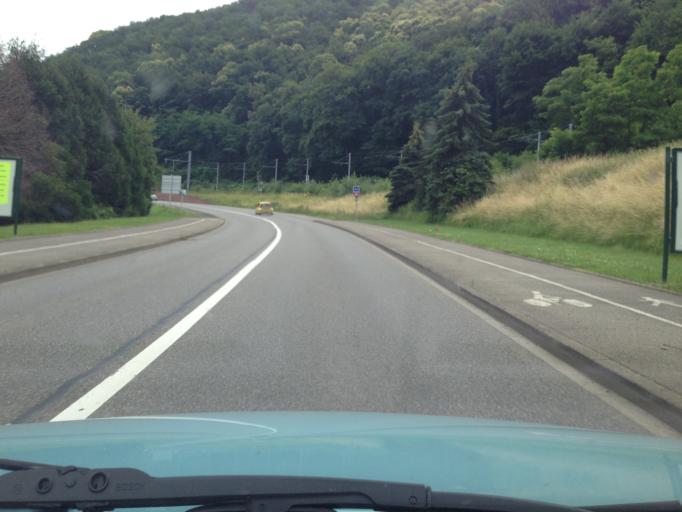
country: FR
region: Alsace
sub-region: Departement du Haut-Rhin
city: Thann
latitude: 47.8150
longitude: 7.0876
